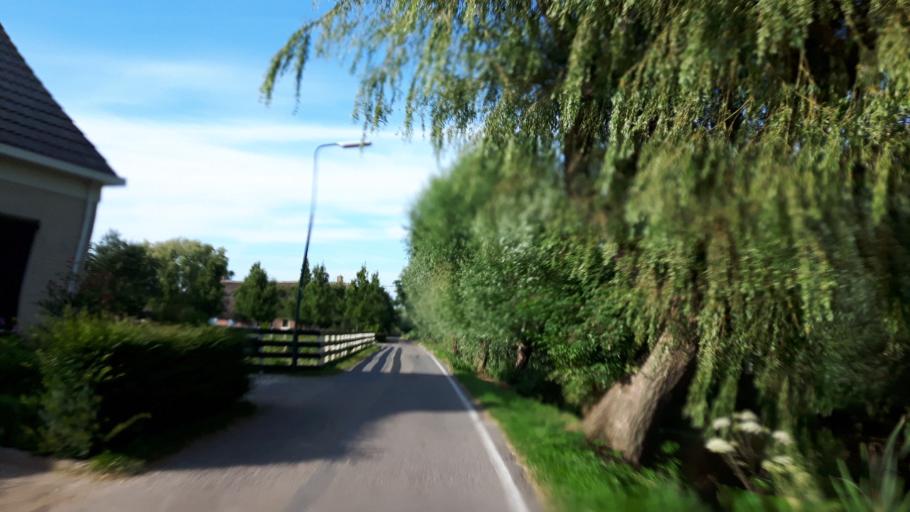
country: NL
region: Utrecht
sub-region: Gemeente Oudewater
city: Oudewater
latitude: 52.0430
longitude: 4.8934
